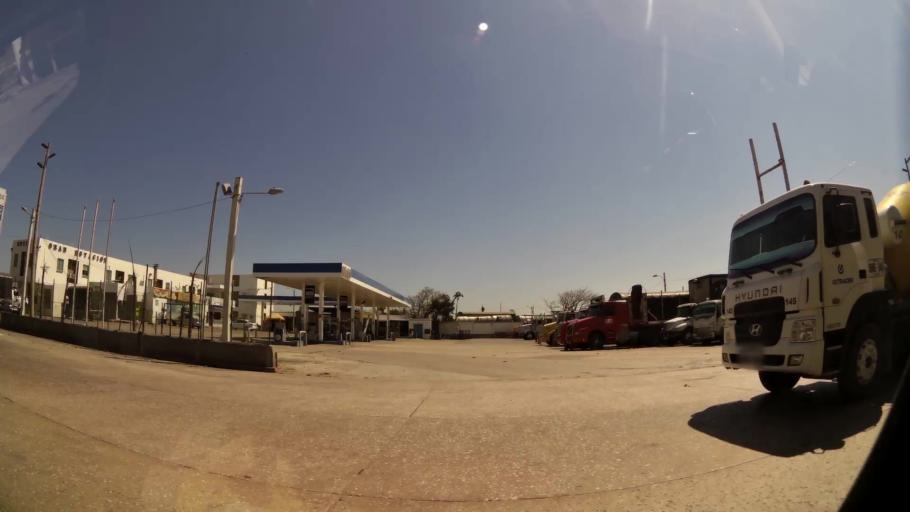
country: CO
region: Atlantico
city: Barranquilla
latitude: 10.9500
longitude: -74.7692
